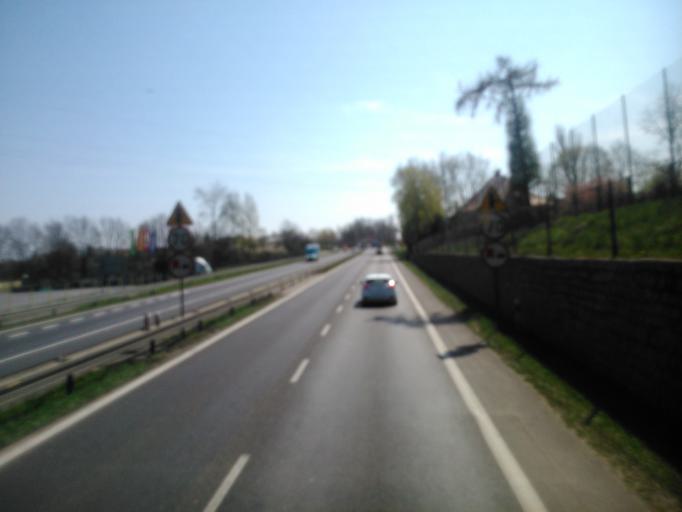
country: PL
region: Silesian Voivodeship
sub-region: Powiat czestochowski
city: Huta Stara B
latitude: 50.7464
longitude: 19.1531
